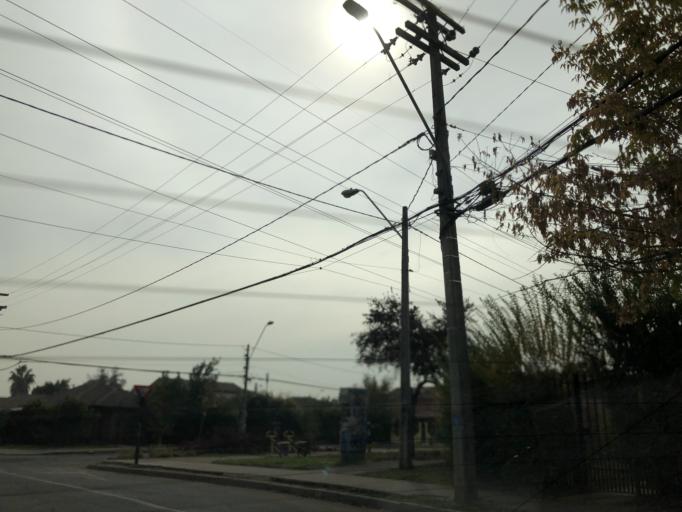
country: CL
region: Santiago Metropolitan
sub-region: Provincia de Cordillera
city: Puente Alto
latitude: -33.5642
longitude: -70.5591
